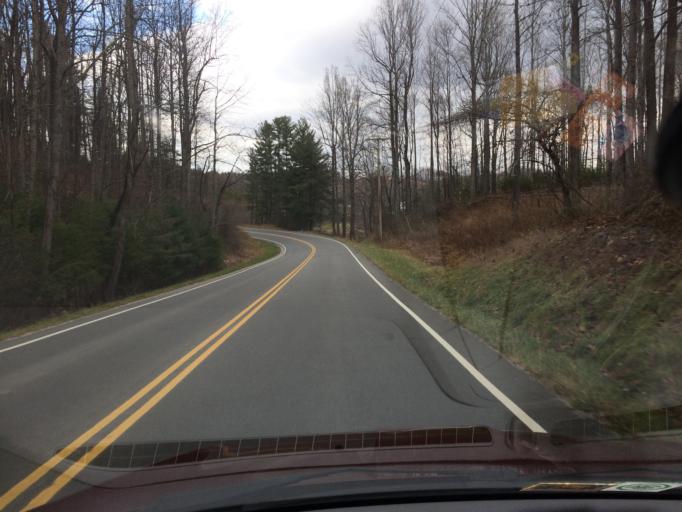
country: US
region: Virginia
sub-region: Patrick County
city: Stuart
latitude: 36.7417
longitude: -80.2510
